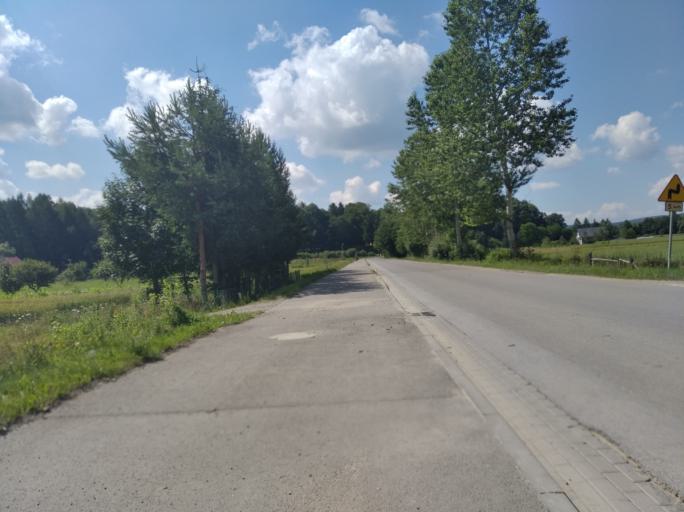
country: PL
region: Subcarpathian Voivodeship
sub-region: Powiat rzeszowski
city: Dynow
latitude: 49.7855
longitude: 22.2382
